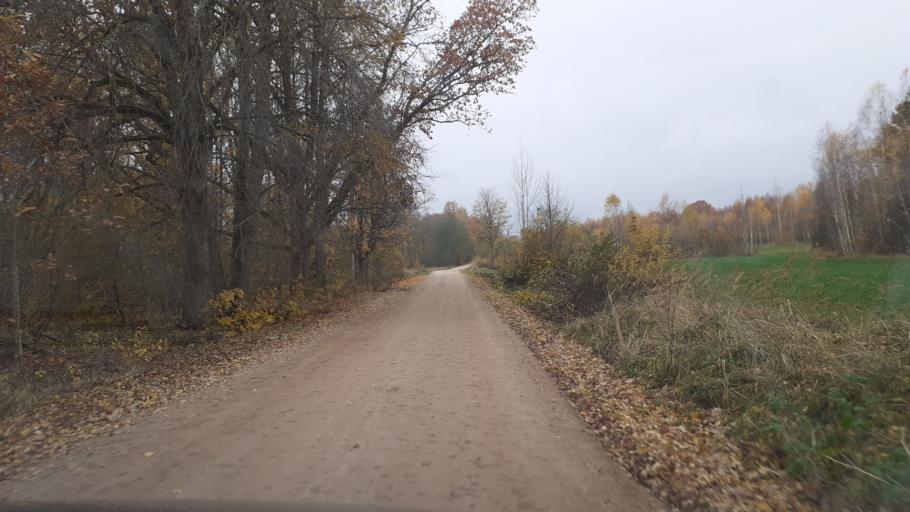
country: LV
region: Saldus Rajons
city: Saldus
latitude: 56.8765
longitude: 22.3049
